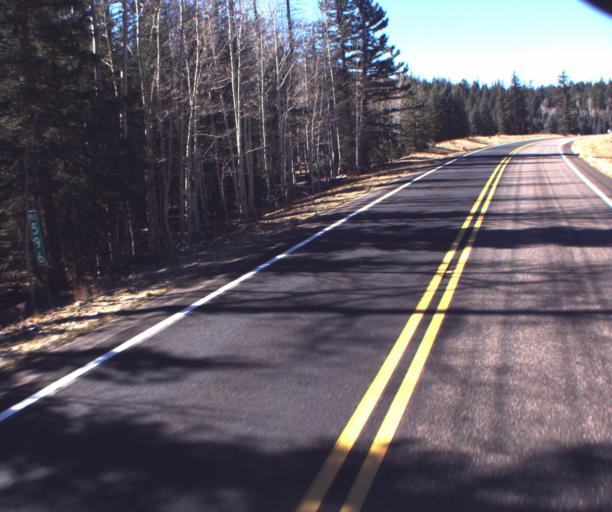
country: US
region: Arizona
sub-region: Coconino County
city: Grand Canyon
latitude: 36.5251
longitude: -112.1455
